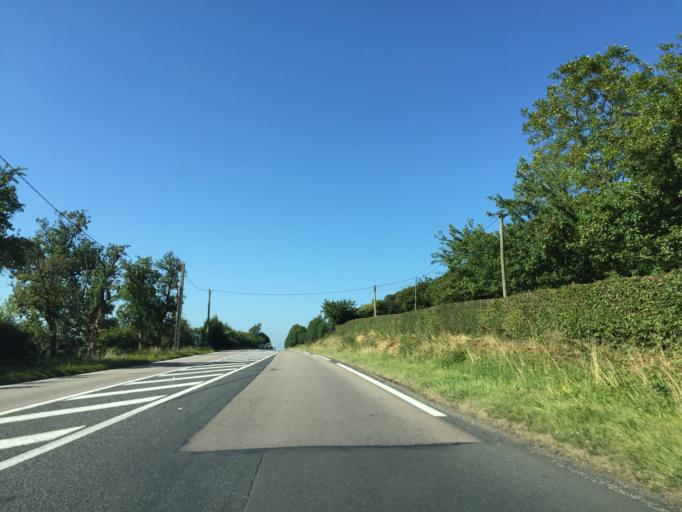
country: FR
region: Lower Normandy
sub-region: Departement du Calvados
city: Lisieux
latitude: 49.1690
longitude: 0.2276
